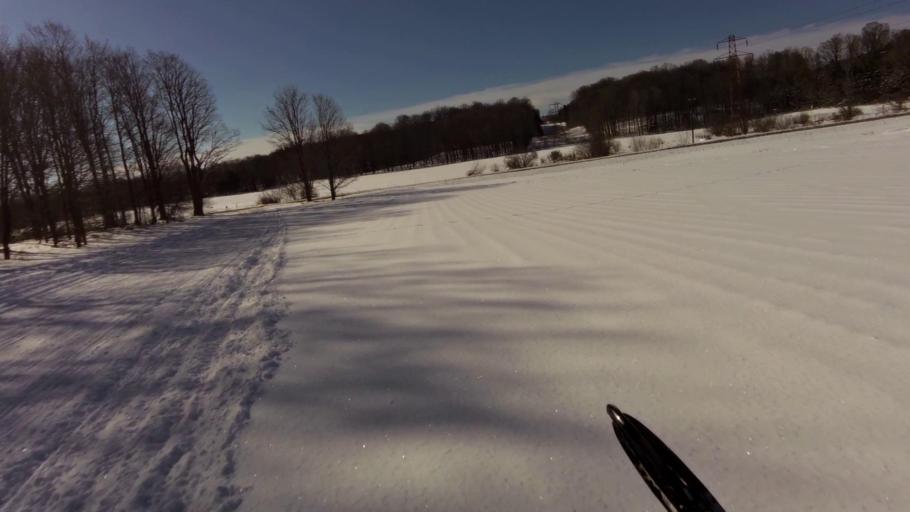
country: US
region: New York
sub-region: Cattaraugus County
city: Franklinville
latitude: 42.3924
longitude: -78.4921
